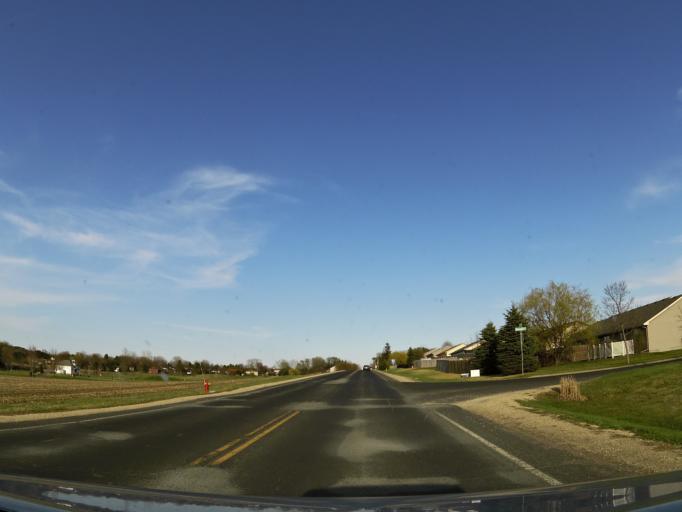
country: US
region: Wisconsin
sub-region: Pierce County
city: River Falls
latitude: 44.8626
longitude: -92.6495
